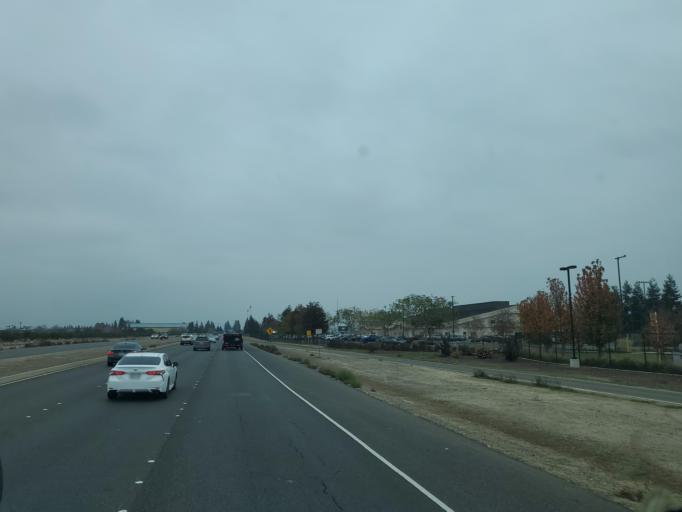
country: US
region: California
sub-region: Stanislaus County
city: Del Rio
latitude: 37.7005
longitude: -121.0090
